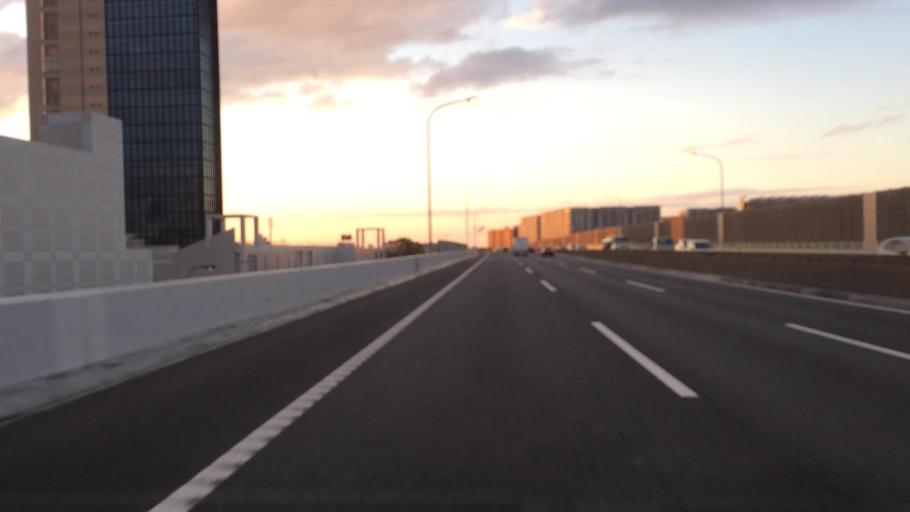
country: JP
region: Chiba
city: Funabashi
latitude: 35.6549
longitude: 140.0422
